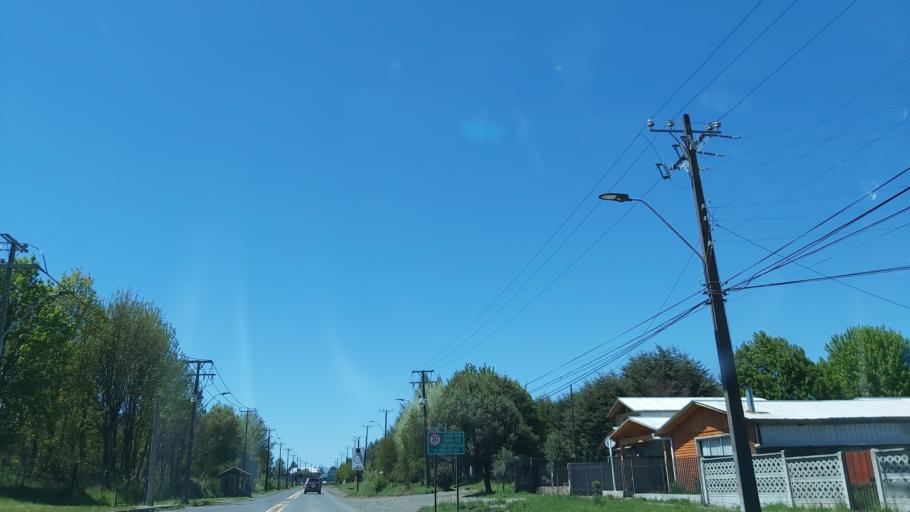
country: CL
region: Araucania
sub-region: Provincia de Cautin
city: Vilcun
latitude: -38.4346
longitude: -71.9026
